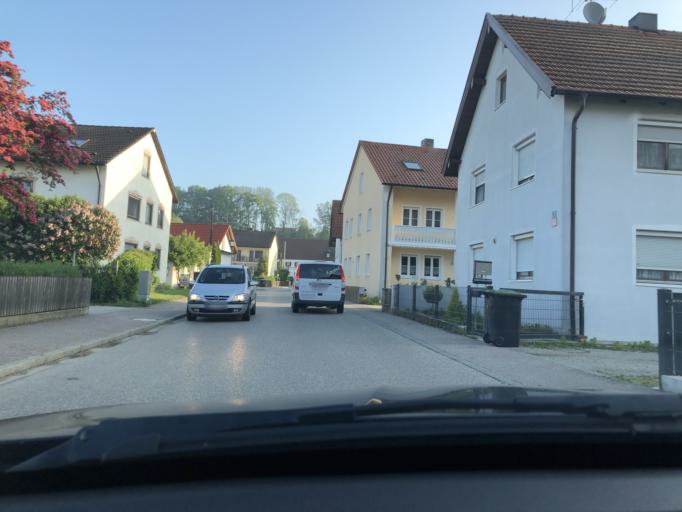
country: DE
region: Bavaria
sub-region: Upper Bavaria
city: Kirchdorf
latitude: 48.4590
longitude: 11.6517
